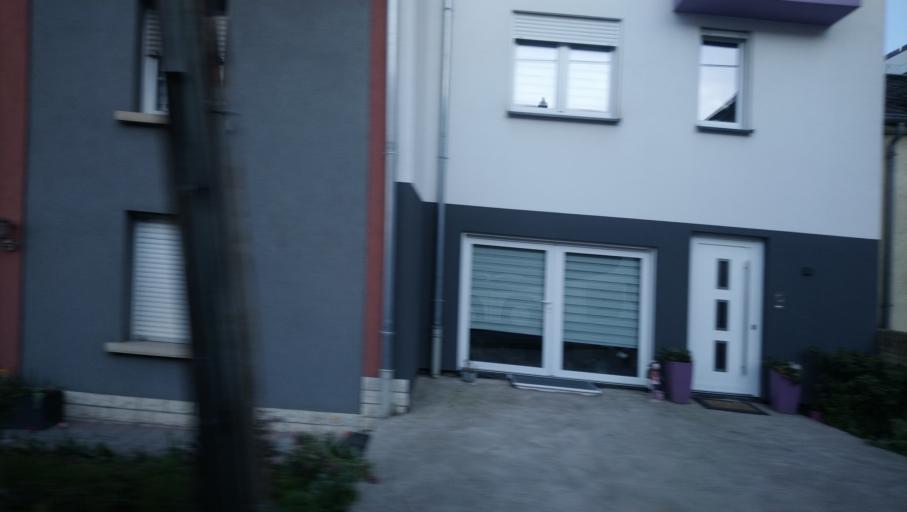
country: LU
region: Luxembourg
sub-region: Canton de Luxembourg
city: Luxembourg
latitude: 49.5956
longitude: 6.1175
